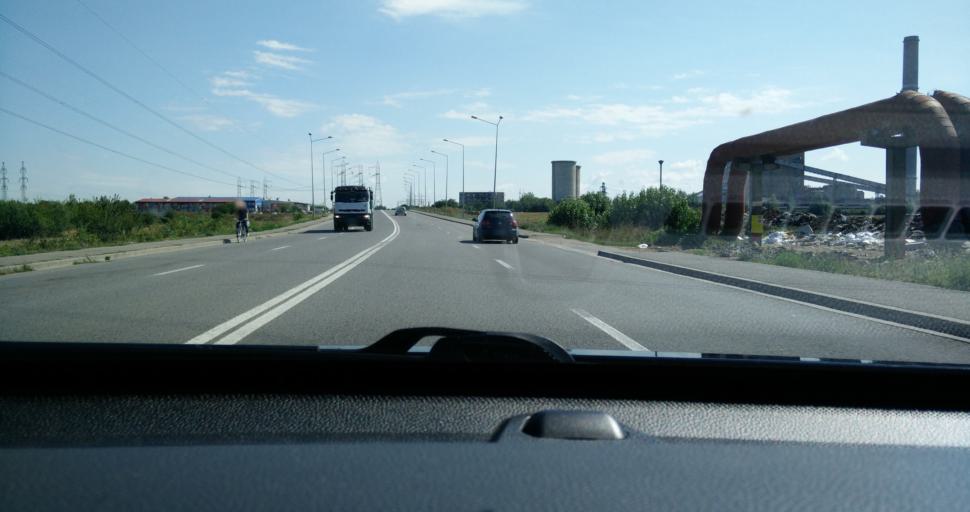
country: RO
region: Bihor
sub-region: Comuna Sanmartin
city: Sanmartin
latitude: 47.0291
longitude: 21.9742
